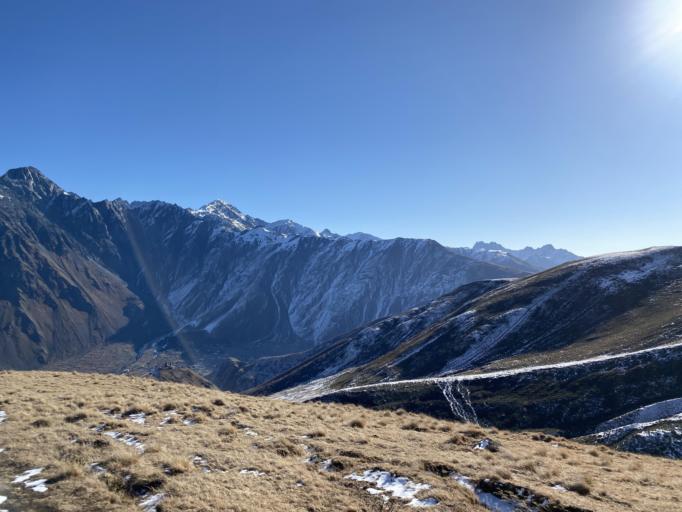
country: GE
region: Mtskheta-Mtianeti
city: Step'antsminda
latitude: 42.6643
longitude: 44.5884
